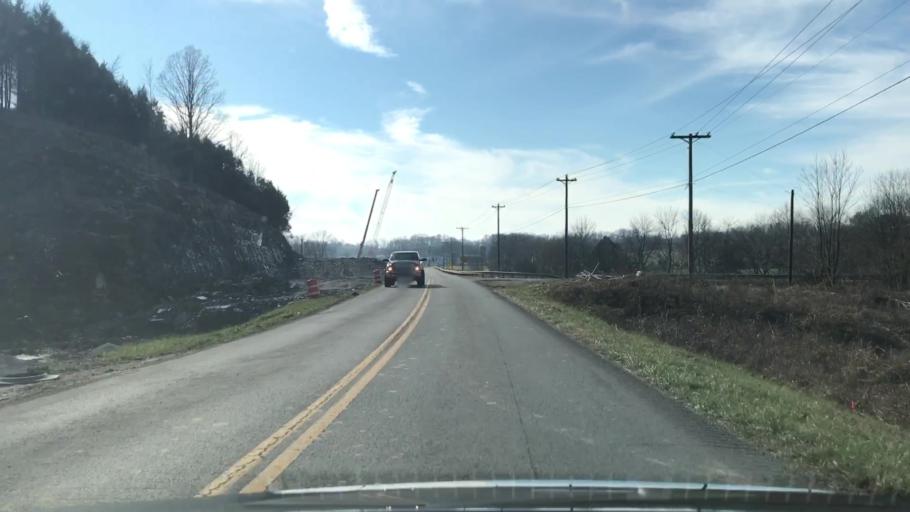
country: US
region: Kentucky
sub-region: Metcalfe County
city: Edmonton
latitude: 36.9329
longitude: -85.6371
